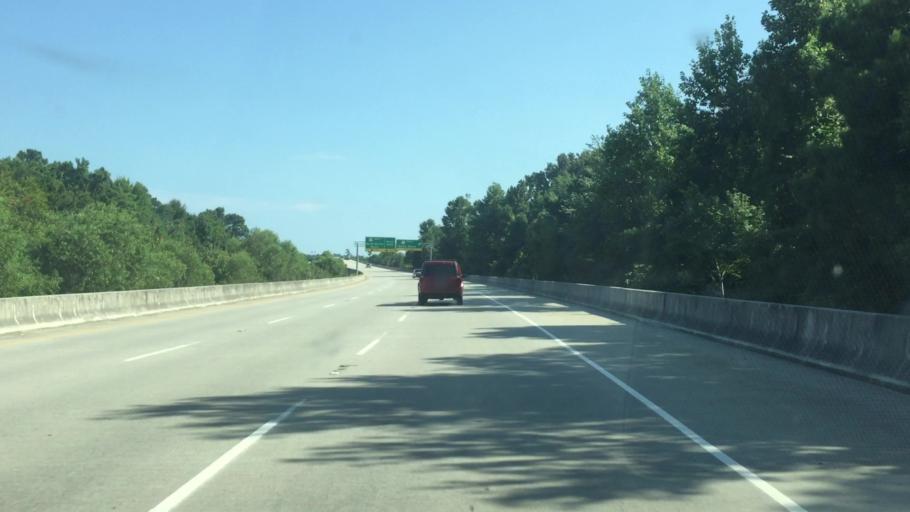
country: US
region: South Carolina
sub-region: Horry County
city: North Myrtle Beach
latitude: 33.7973
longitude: -78.7794
